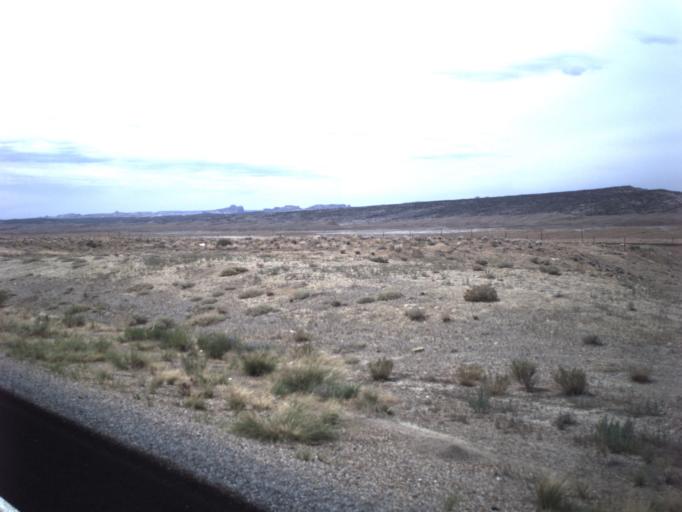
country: US
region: Utah
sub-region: Carbon County
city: East Carbon City
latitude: 39.1836
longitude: -110.3384
